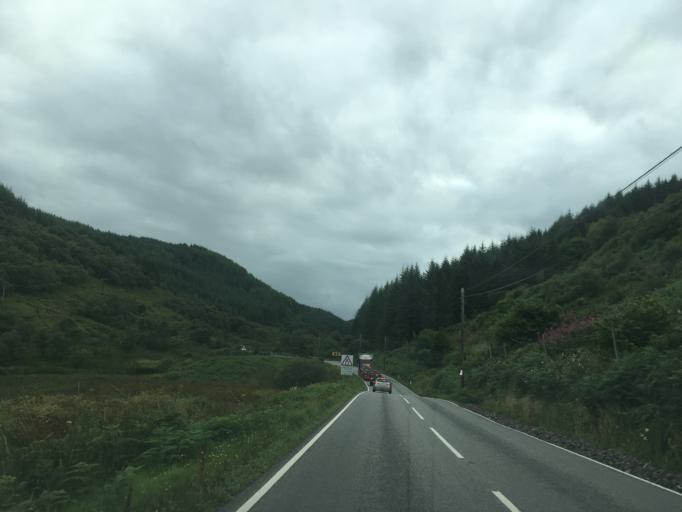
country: GB
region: Scotland
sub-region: Argyll and Bute
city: Oban
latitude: 56.2945
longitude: -5.4672
